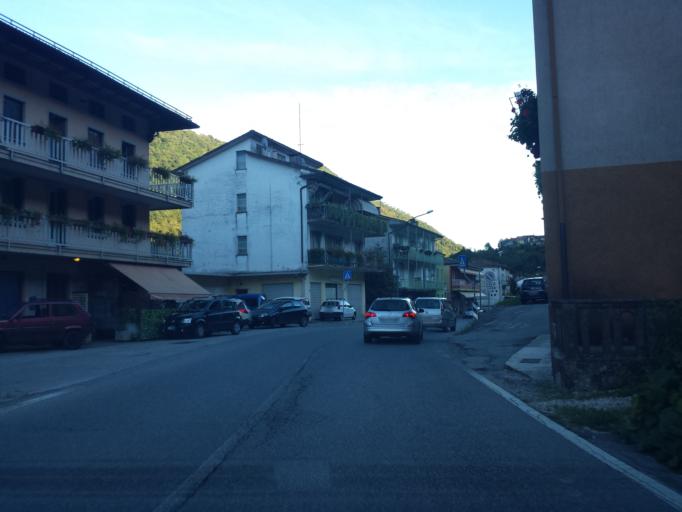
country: IT
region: Veneto
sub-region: Provincia di Vicenza
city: San Quirico
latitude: 45.6886
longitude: 11.2629
